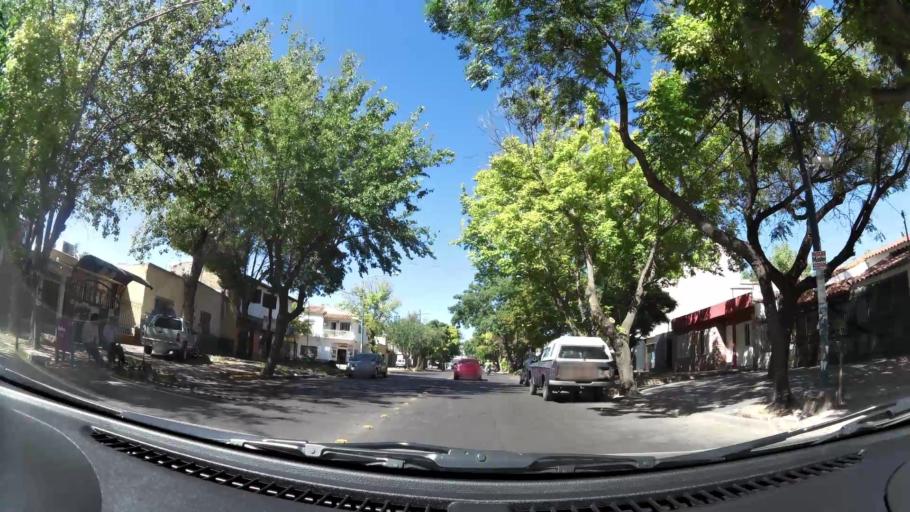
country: AR
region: Mendoza
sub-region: Departamento de Godoy Cruz
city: Godoy Cruz
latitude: -32.9205
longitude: -68.8596
